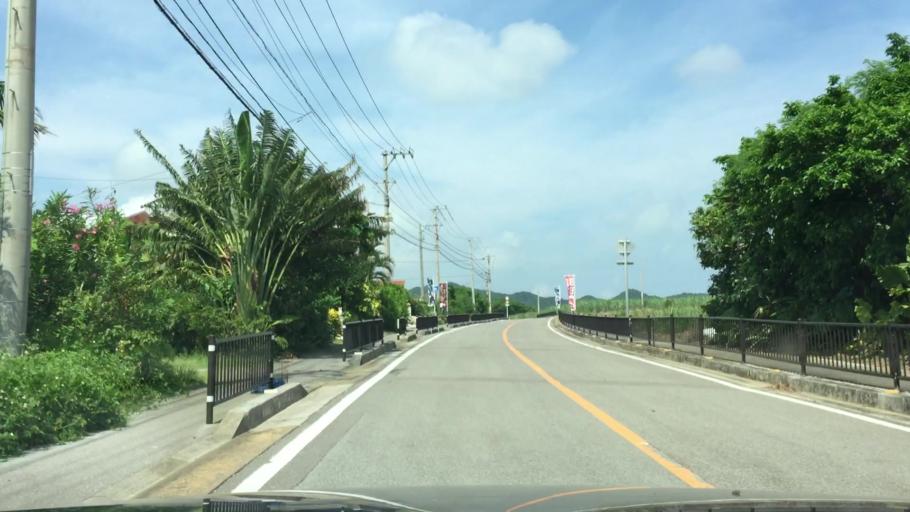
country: JP
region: Okinawa
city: Ishigaki
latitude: 24.4982
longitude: 124.2401
